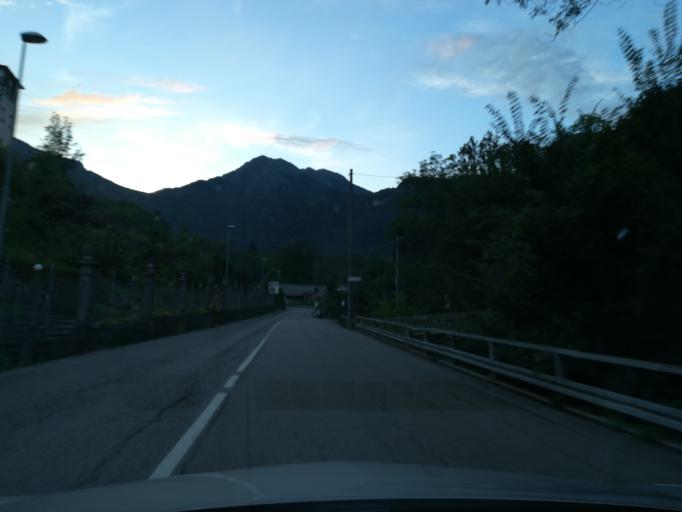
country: IT
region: Lombardy
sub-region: Provincia di Bergamo
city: Rota d'Imagna
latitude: 45.8219
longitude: 9.5114
